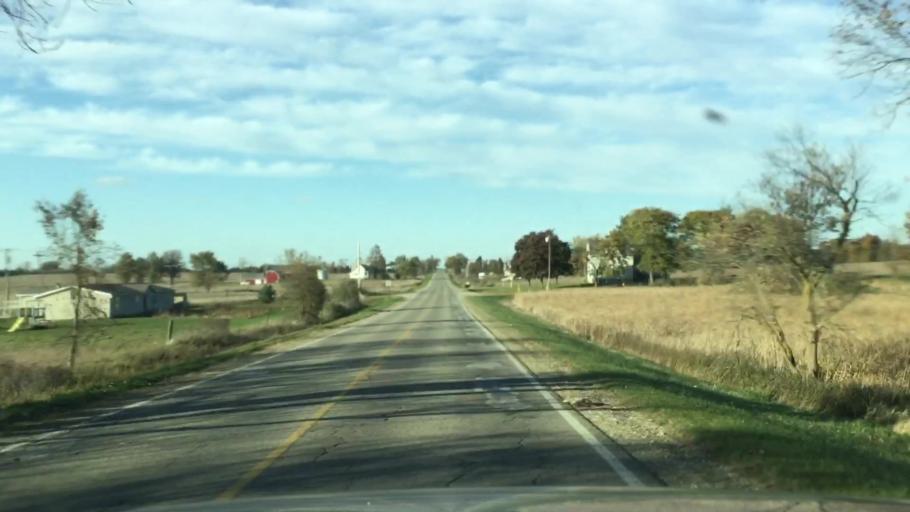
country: US
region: Michigan
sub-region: Lapeer County
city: North Branch
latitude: 43.2515
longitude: -83.1976
